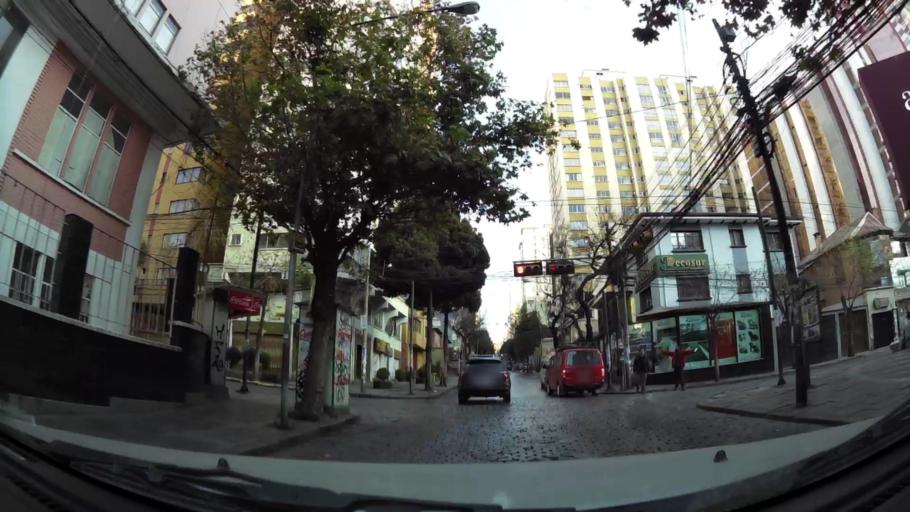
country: BO
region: La Paz
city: La Paz
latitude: -16.5082
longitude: -68.1285
